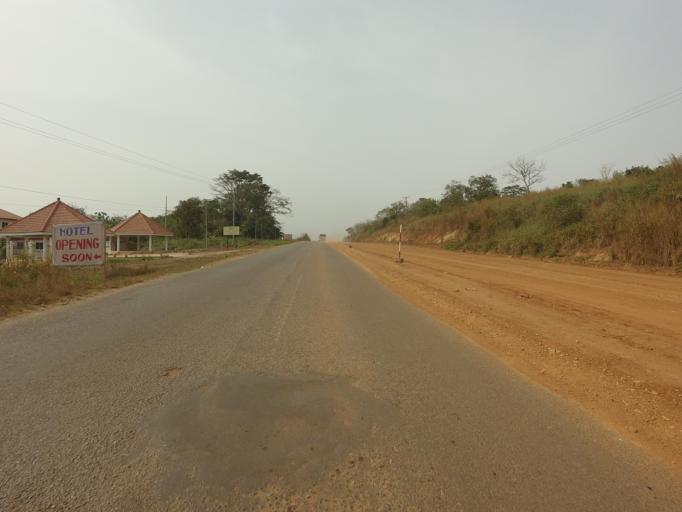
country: GH
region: Volta
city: Ho
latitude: 6.5881
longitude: 0.4298
